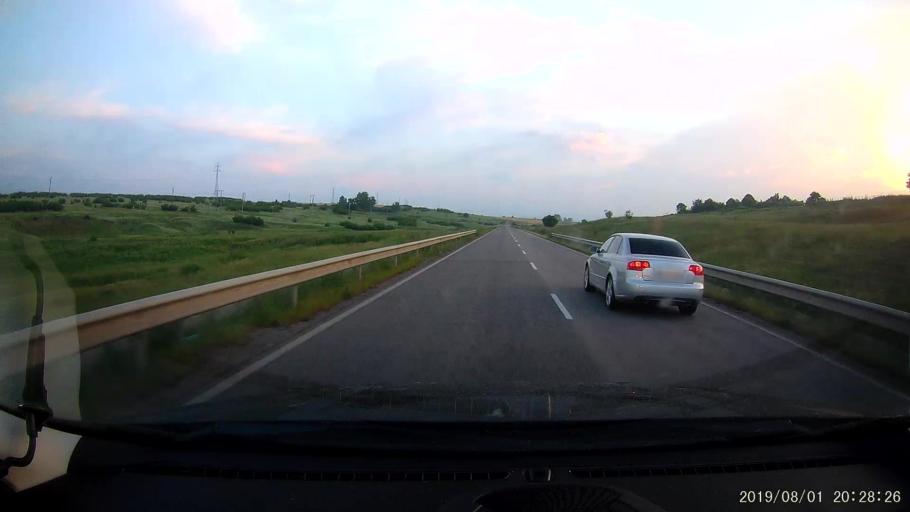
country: BG
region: Yambol
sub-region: Obshtina Elkhovo
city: Elkhovo
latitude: 42.1687
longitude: 26.5779
